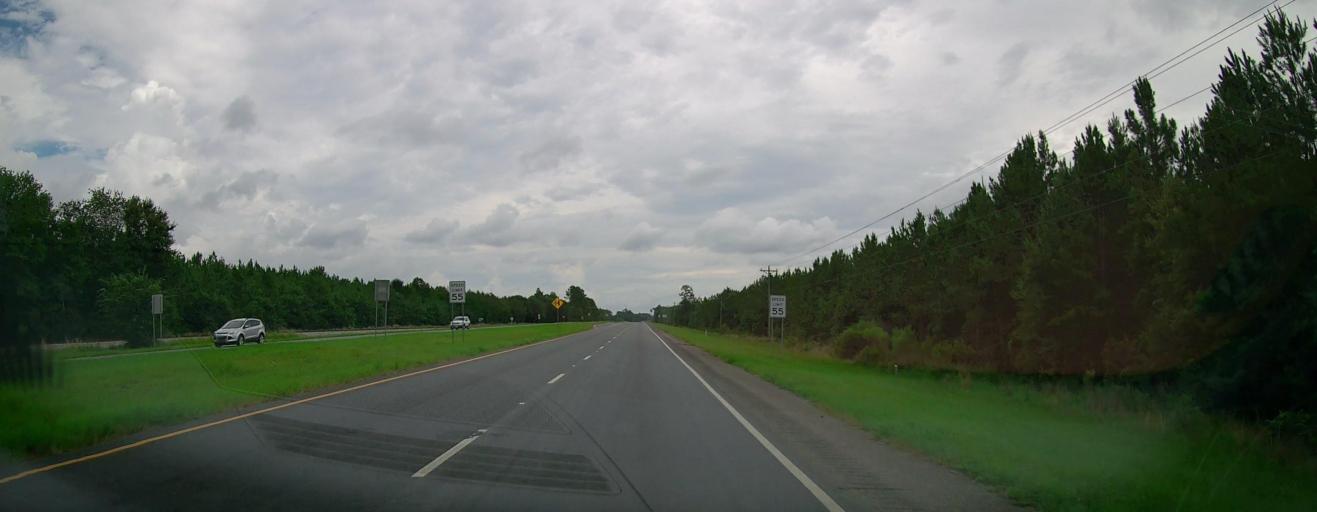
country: US
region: Georgia
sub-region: Dodge County
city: Eastman
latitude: 32.1082
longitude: -83.0877
